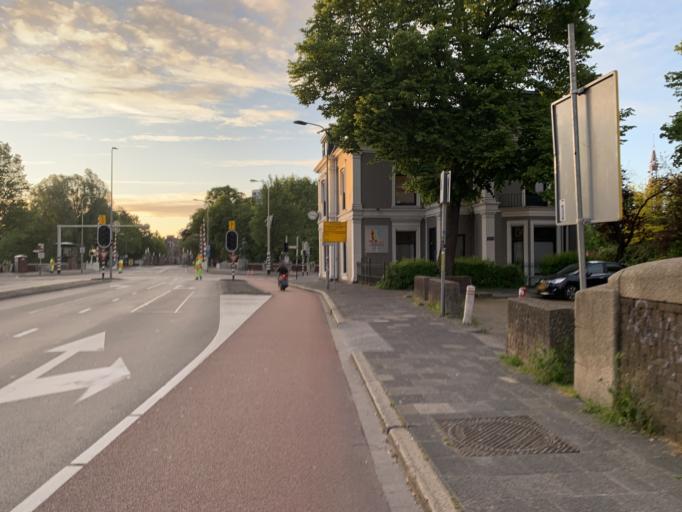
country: NL
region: Groningen
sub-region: Gemeente Groningen
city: Groningen
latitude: 53.2118
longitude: 6.5709
